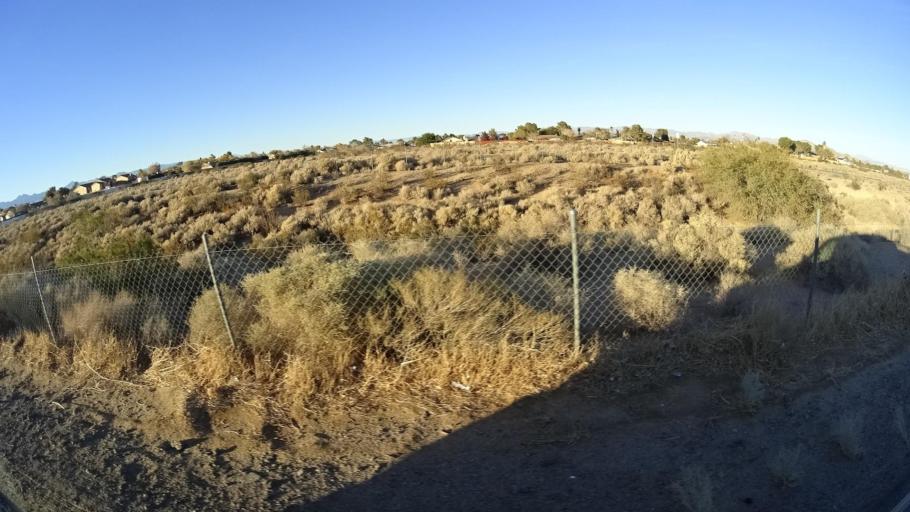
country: US
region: California
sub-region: Kern County
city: Ridgecrest
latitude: 35.6077
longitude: -117.6758
